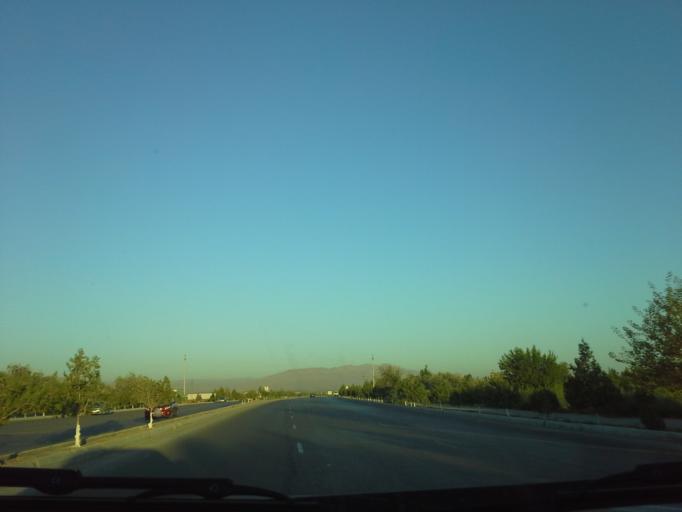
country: TM
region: Ahal
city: Abadan
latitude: 38.1037
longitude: 58.1361
